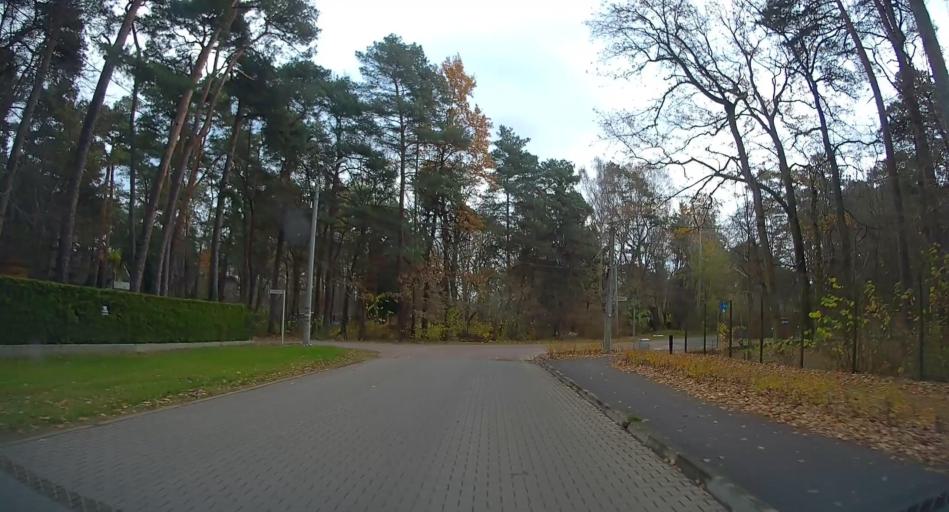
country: PL
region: Masovian Voivodeship
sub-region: Powiat piaseczynski
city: Zabieniec
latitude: 52.0539
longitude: 21.0217
